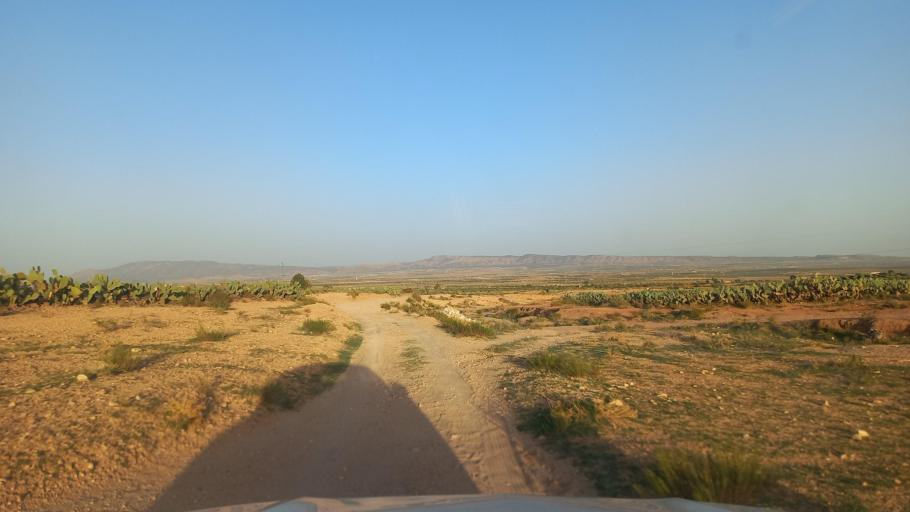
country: TN
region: Al Qasrayn
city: Sbiba
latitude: 35.3724
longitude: 9.0068
